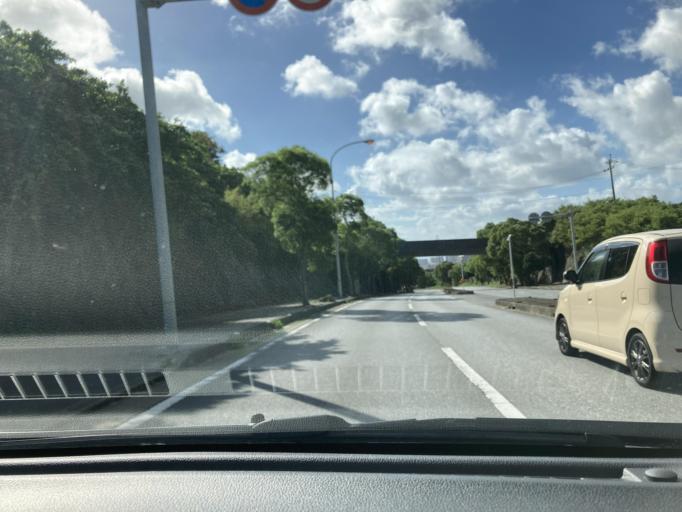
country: JP
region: Okinawa
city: Itoman
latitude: 26.1525
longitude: 127.6818
